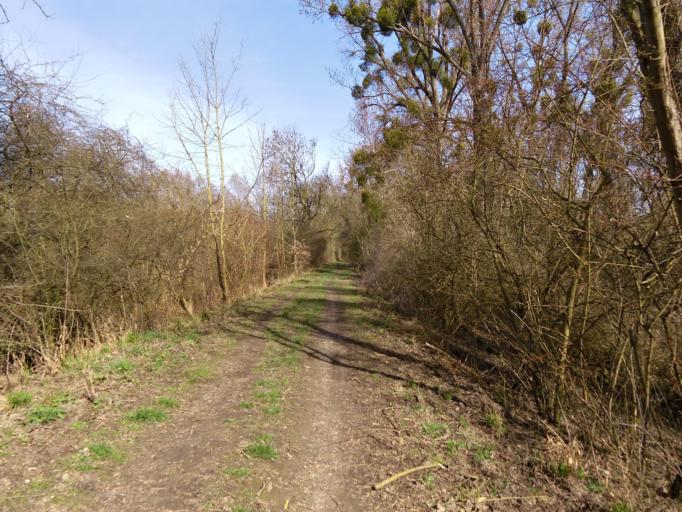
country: DE
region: Hesse
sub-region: Regierungsbezirk Darmstadt
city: Stockstadt am Rhein
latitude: 49.8175
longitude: 8.4169
